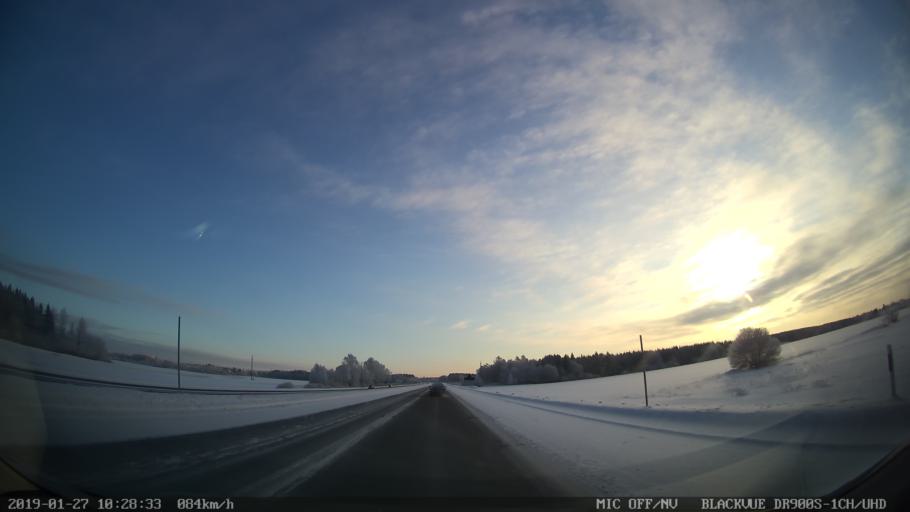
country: EE
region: Harju
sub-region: Raasiku vald
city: Raasiku
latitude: 59.4386
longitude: 25.1459
